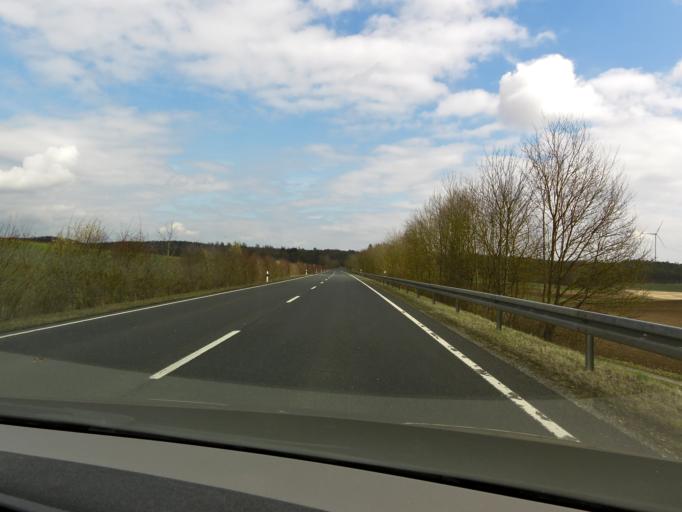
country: DE
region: Bavaria
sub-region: Regierungsbezirk Unterfranken
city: Arnstein
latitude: 49.9997
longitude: 10.0100
